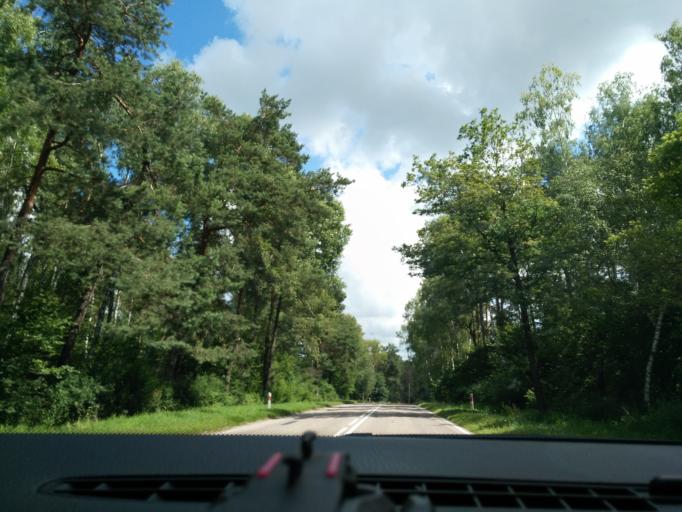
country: PL
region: Podlasie
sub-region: Powiat siemiatycki
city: Dziadkowice
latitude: 52.5920
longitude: 22.9493
